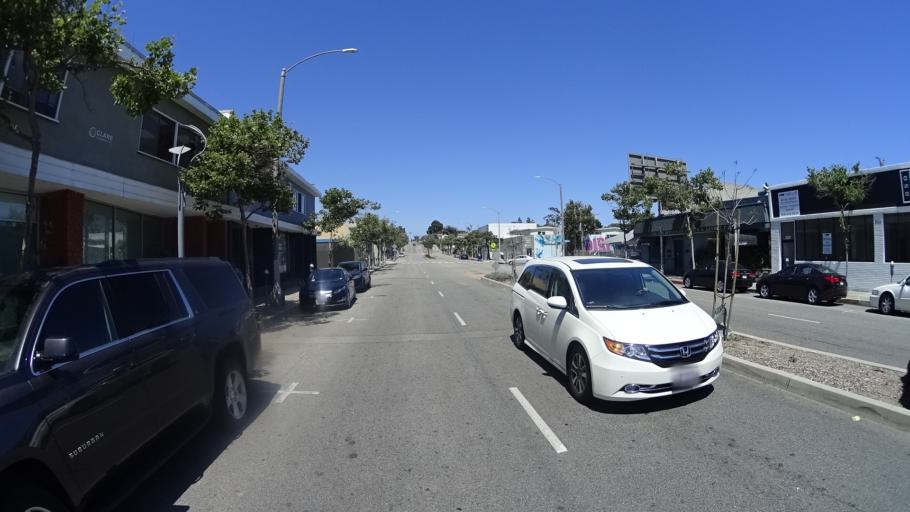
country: US
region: California
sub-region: Los Angeles County
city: Santa Monica
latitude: 34.0131
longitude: -118.4816
